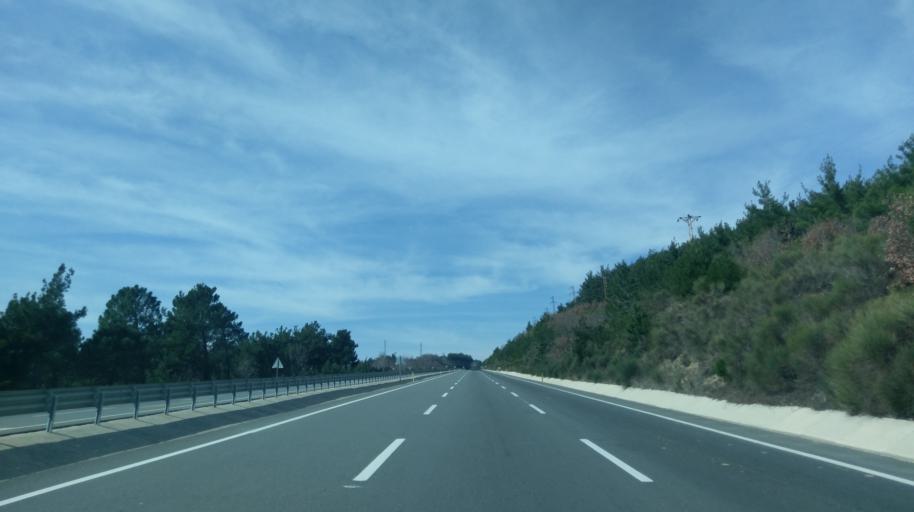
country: TR
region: Canakkale
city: Evrese
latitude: 40.7080
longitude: 26.7793
